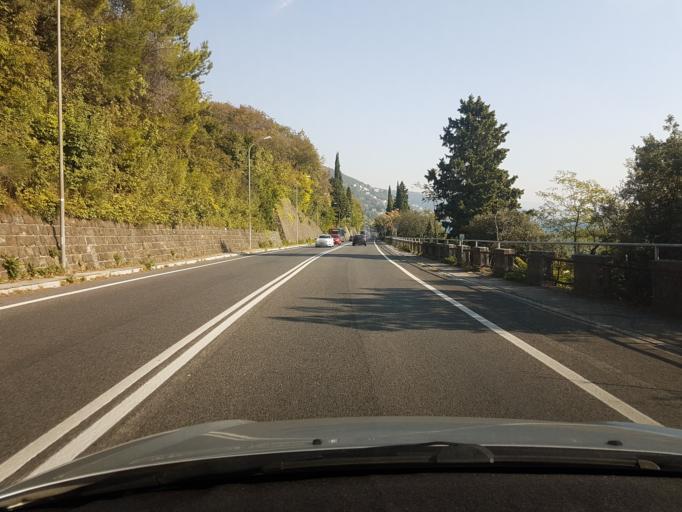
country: IT
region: Friuli Venezia Giulia
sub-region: Provincia di Trieste
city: Prosecco-Contovello
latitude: 45.7014
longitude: 13.7215
